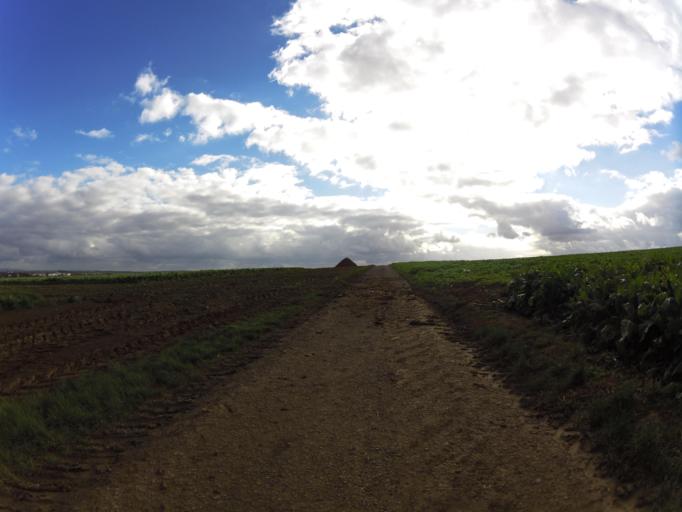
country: DE
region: Bavaria
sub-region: Regierungsbezirk Unterfranken
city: Unterpleichfeld
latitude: 49.8776
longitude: 10.0115
